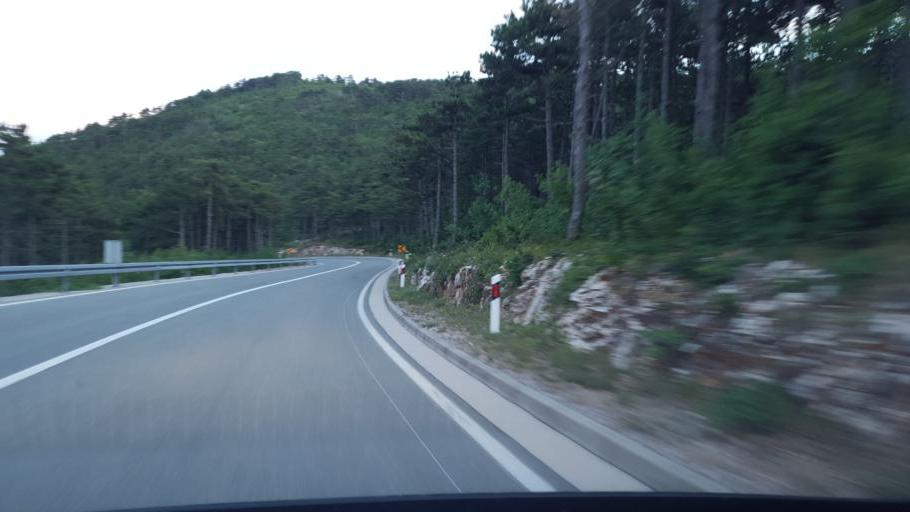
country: HR
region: Primorsko-Goranska
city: Punat
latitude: 45.0291
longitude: 14.6737
